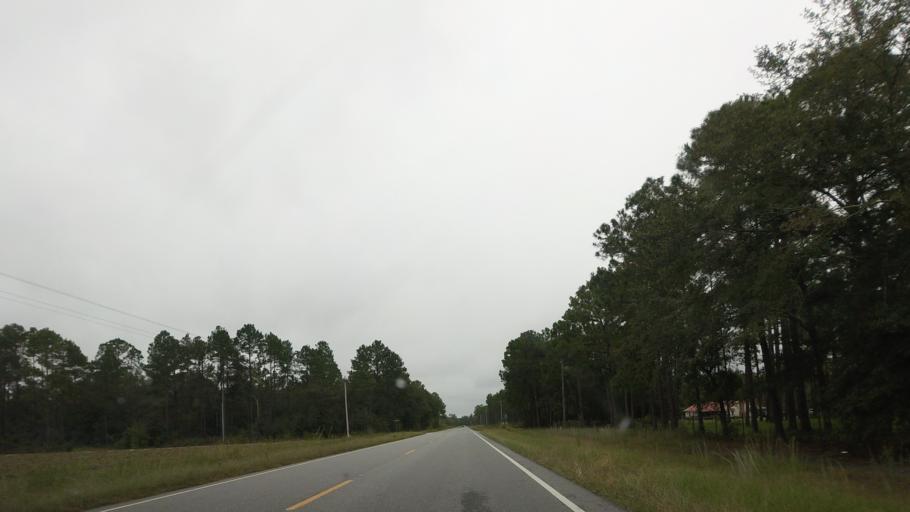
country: US
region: Georgia
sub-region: Berrien County
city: Nashville
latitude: 31.2911
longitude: -83.2372
